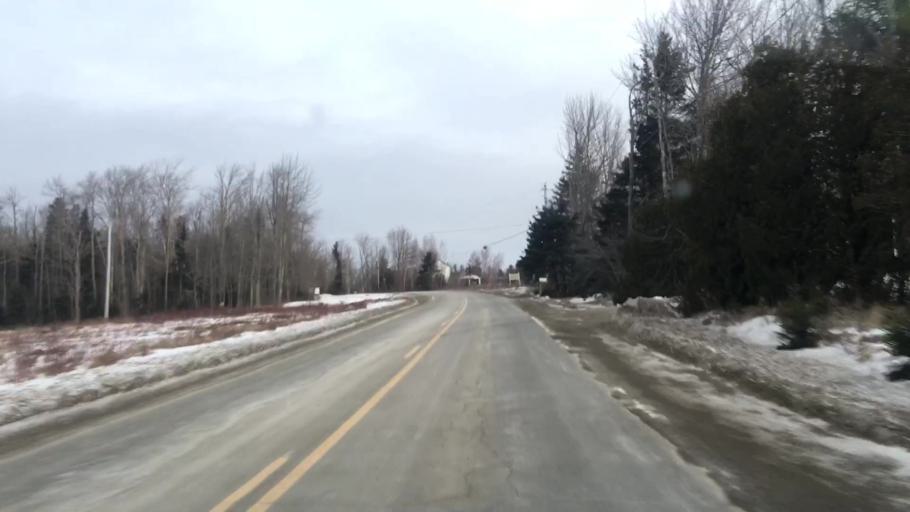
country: US
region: Maine
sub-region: Hancock County
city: Franklin
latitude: 44.7229
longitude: -68.3346
